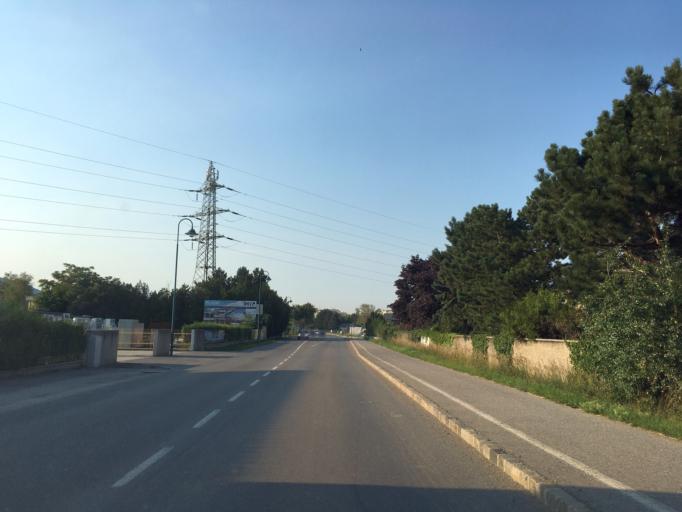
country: AT
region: Lower Austria
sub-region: Politischer Bezirk Baden
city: Kottingbrunn
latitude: 47.9499
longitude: 16.2223
